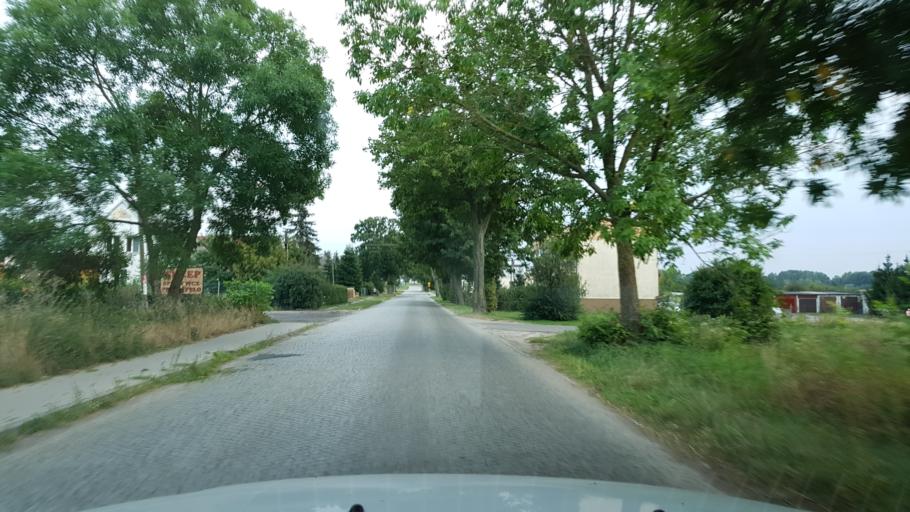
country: PL
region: West Pomeranian Voivodeship
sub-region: Powiat koszalinski
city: Mielno
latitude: 54.2252
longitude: 16.0248
